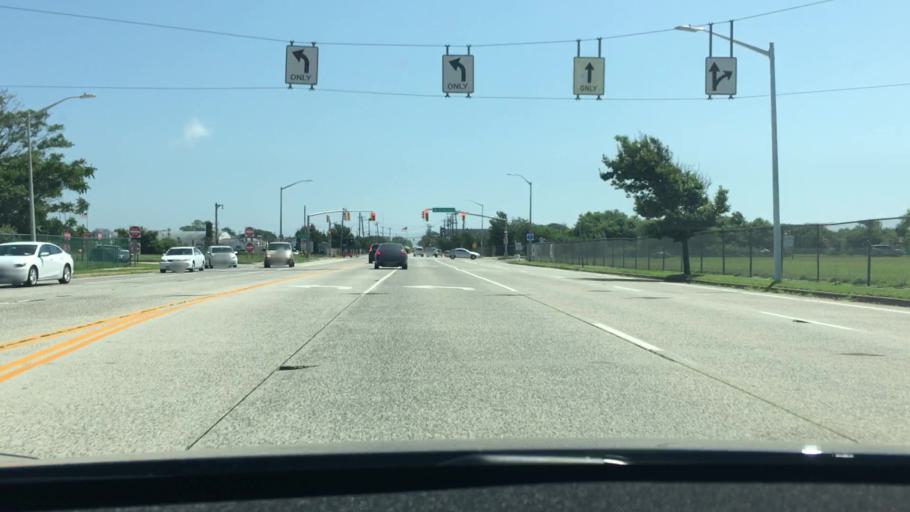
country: US
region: New York
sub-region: Nassau County
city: Point Lookout
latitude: 40.5920
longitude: -73.5885
